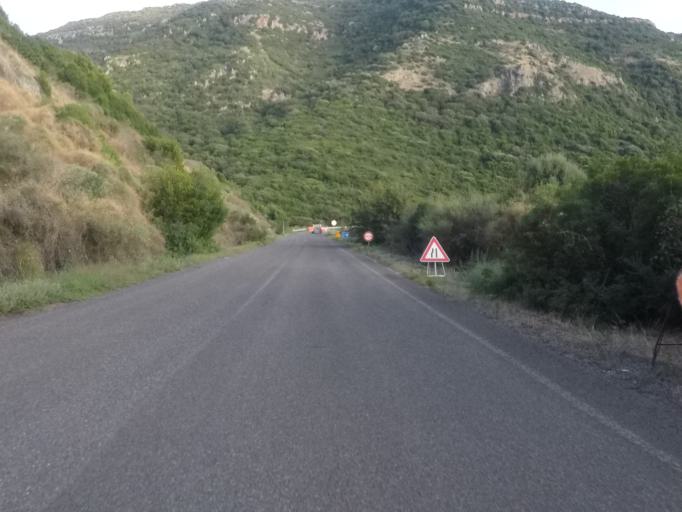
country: IT
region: Sardinia
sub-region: Provincia di Oristano
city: Montresta
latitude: 40.4075
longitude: 8.4119
